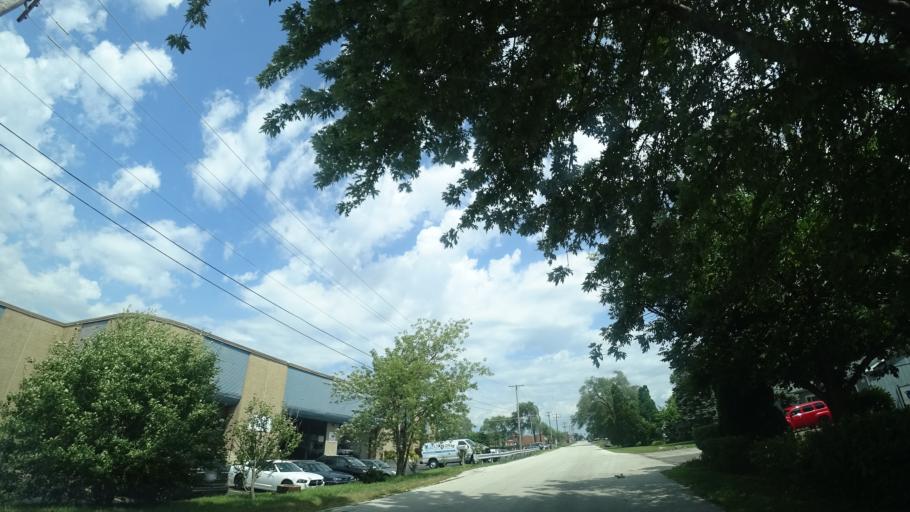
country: US
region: Illinois
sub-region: Cook County
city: Alsip
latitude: 41.6690
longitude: -87.7437
